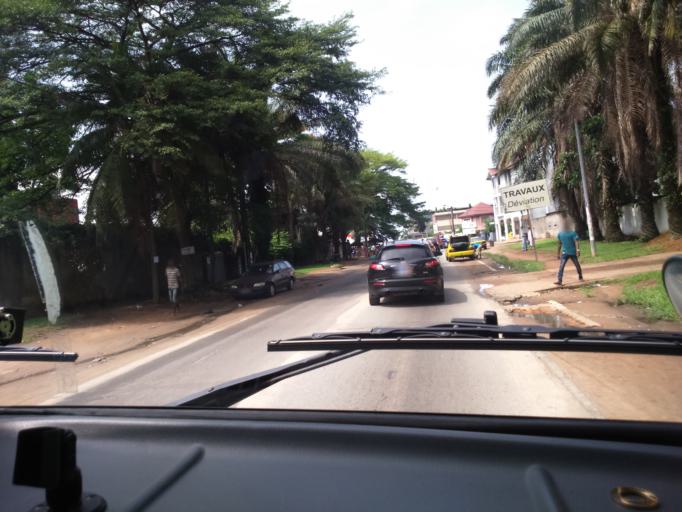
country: CI
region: Lagunes
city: Abidjan
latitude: 5.3579
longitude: -3.9783
